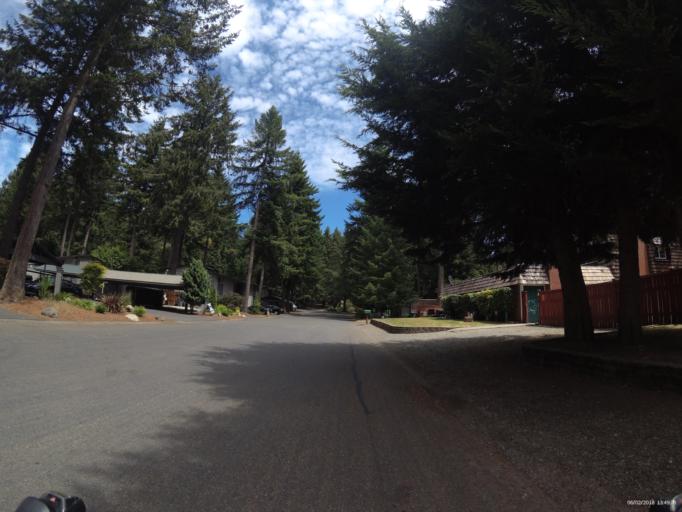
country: US
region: Washington
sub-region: Pierce County
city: University Place
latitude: 47.2102
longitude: -122.5667
